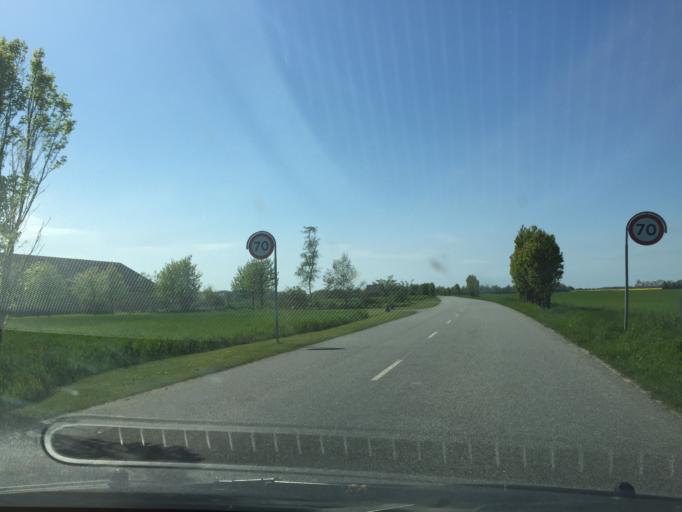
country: DK
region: Zealand
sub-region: Lolland Kommune
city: Rodbyhavn
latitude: 54.6703
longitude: 11.3565
